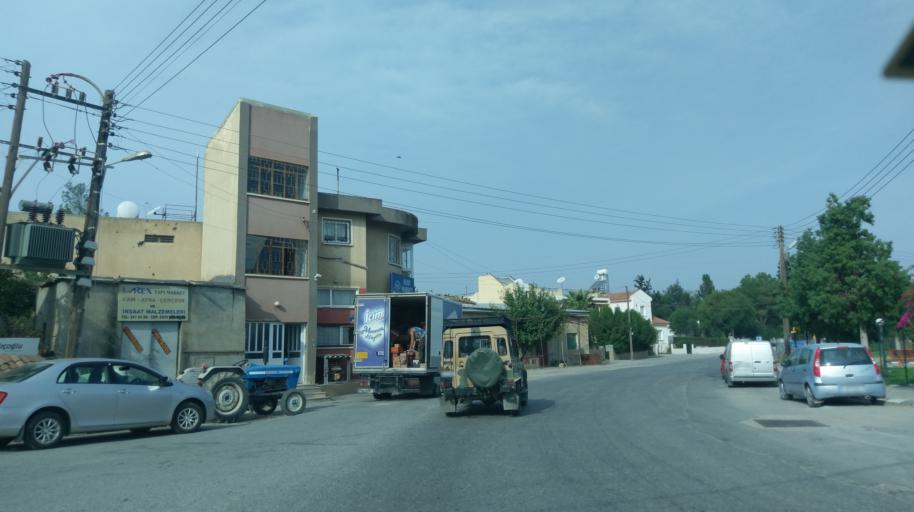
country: CY
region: Lefkosia
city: Mammari
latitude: 35.2312
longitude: 33.1652
